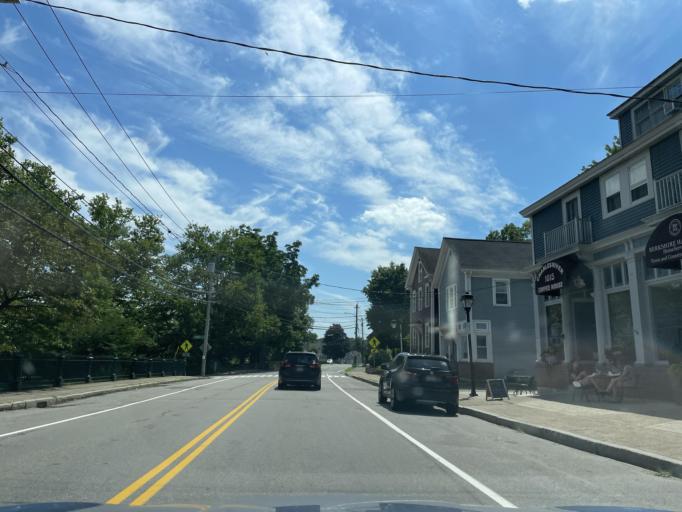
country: US
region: Massachusetts
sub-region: Norfolk County
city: Wellesley
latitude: 42.2723
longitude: -71.3164
